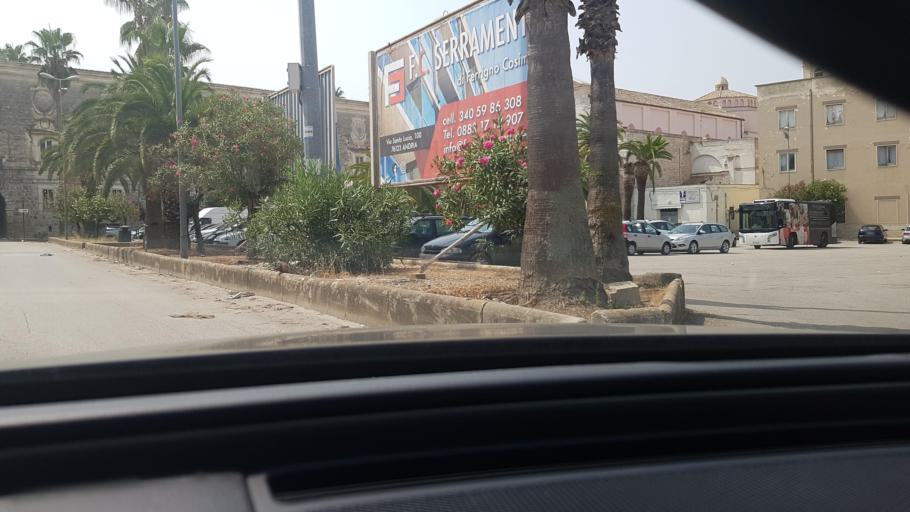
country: IT
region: Apulia
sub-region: Provincia di Barletta - Andria - Trani
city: Andria
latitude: 41.2329
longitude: 16.2685
